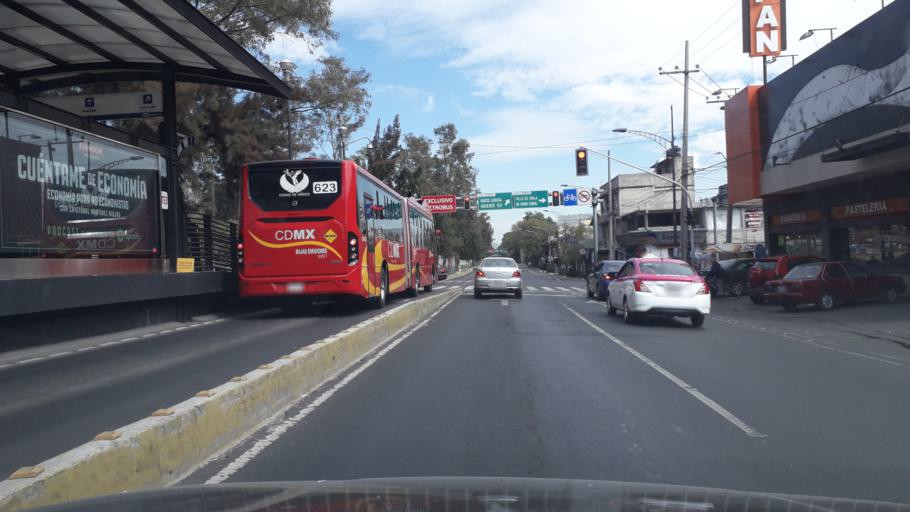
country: MX
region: Mexico City
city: Gustavo A. Madero
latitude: 19.4932
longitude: -99.0915
